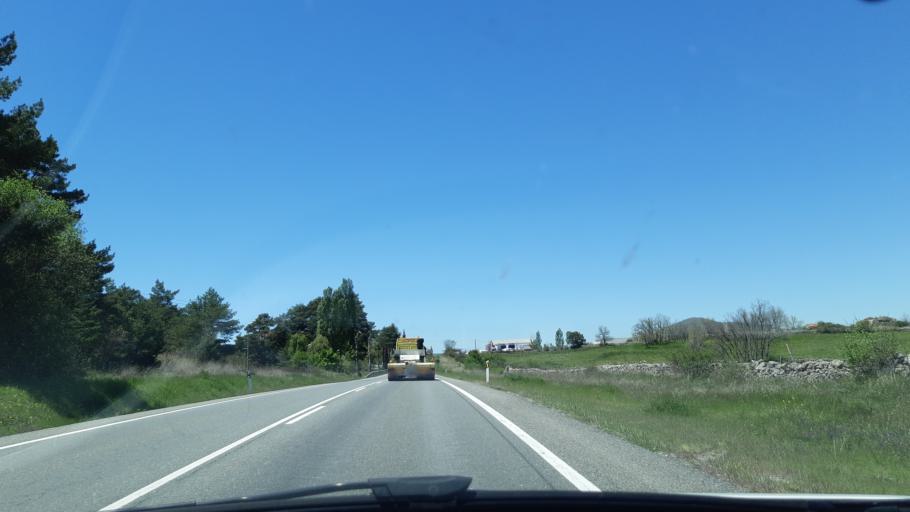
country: ES
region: Castille and Leon
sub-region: Provincia de Avila
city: Peguerinos
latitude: 40.7166
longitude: -4.2026
